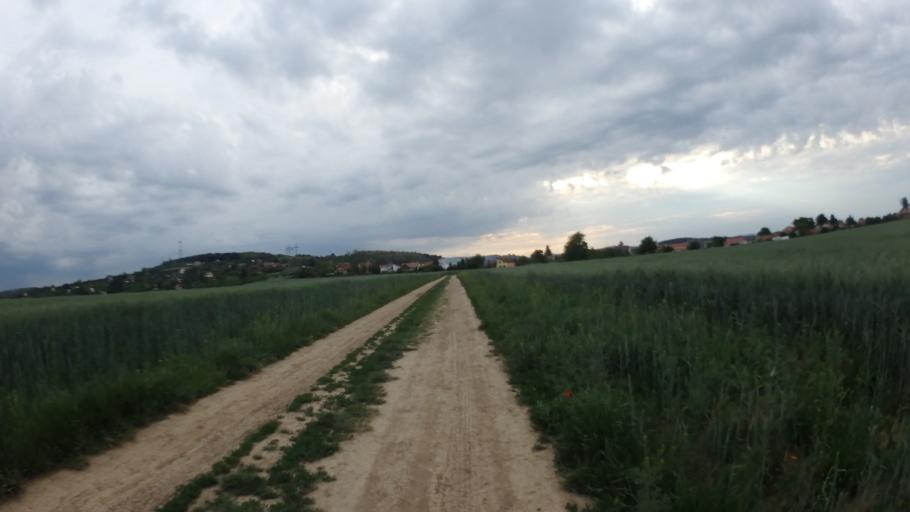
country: CZ
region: South Moravian
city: Moravany
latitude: 49.1391
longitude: 16.5588
